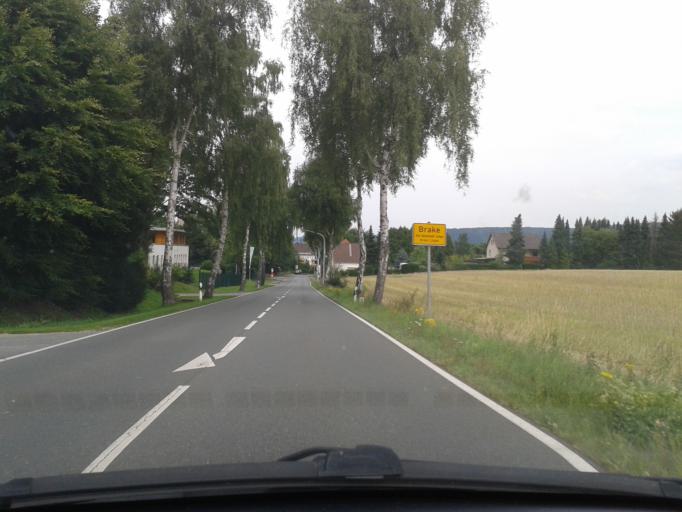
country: DE
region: North Rhine-Westphalia
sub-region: Regierungsbezirk Detmold
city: Lemgo
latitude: 52.0099
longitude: 8.9191
